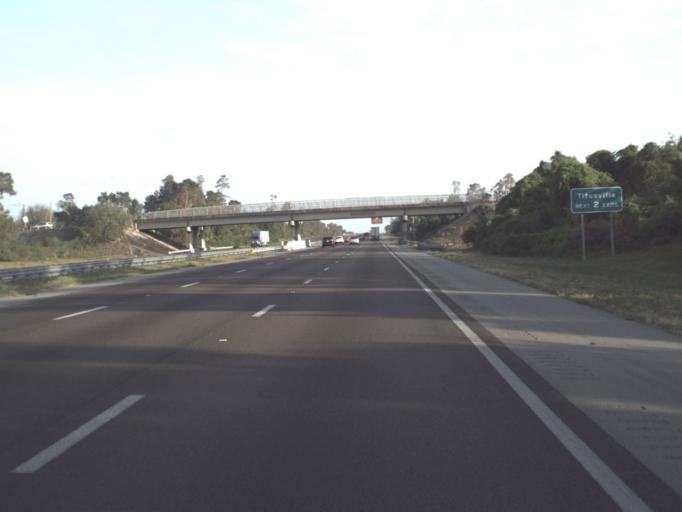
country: US
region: Florida
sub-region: Brevard County
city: Mims
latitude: 28.6387
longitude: -80.8586
